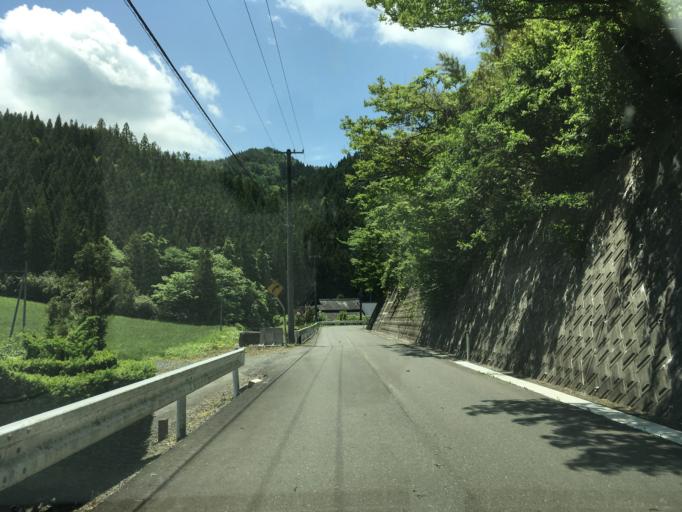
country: JP
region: Miyagi
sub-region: Oshika Gun
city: Onagawa Cho
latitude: 38.6733
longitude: 141.3624
